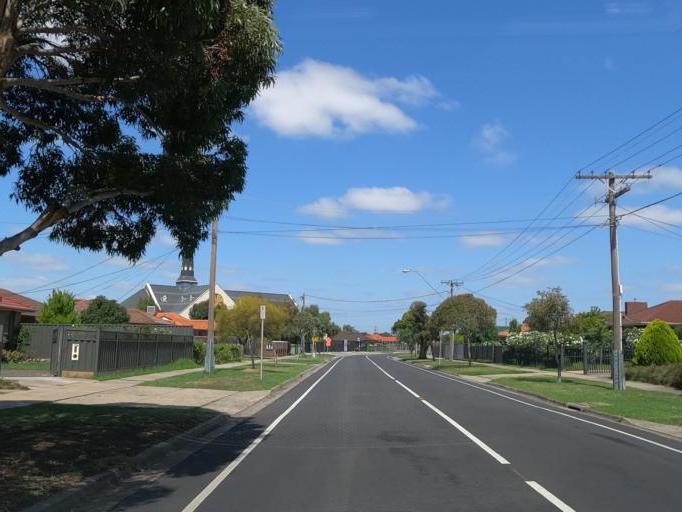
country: AU
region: Victoria
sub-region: Hume
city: Gladstone Park
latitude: -37.6916
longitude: 144.8910
